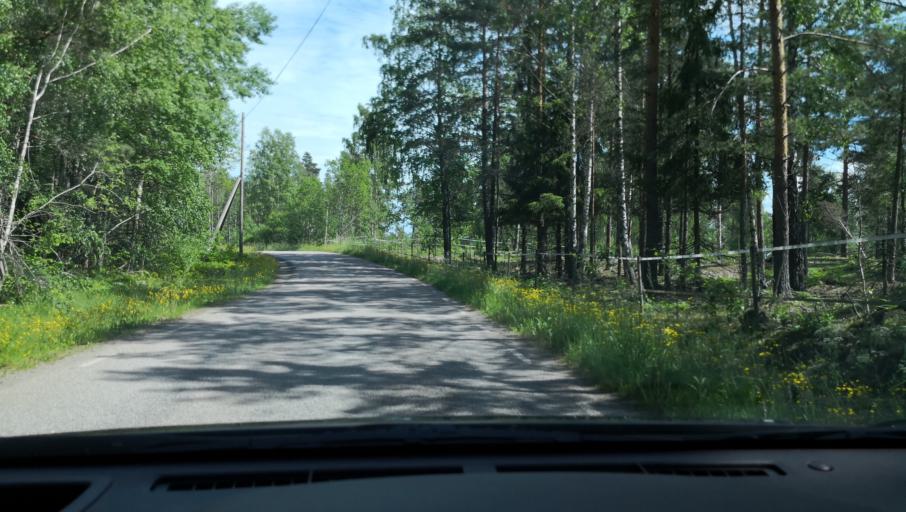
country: SE
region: Uppsala
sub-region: Uppsala Kommun
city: Alsike
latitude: 59.7037
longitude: 17.6938
